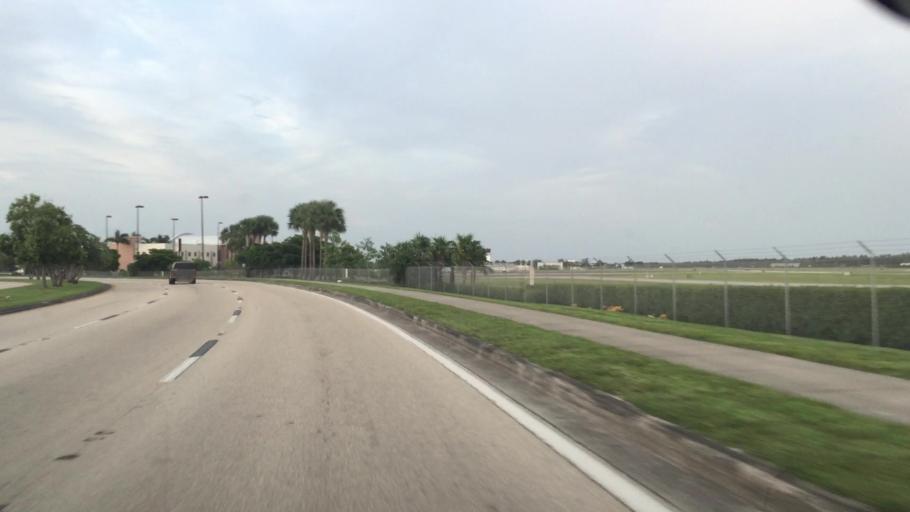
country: US
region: Florida
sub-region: Lee County
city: Pine Manor
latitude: 26.5843
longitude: -81.8689
